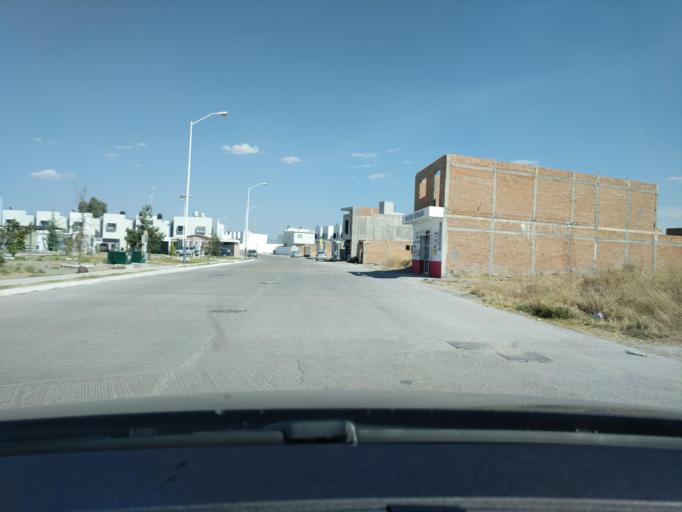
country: MX
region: Durango
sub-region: Durango
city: Sebastian Lerdo de Tejada
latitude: 23.9987
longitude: -104.6072
